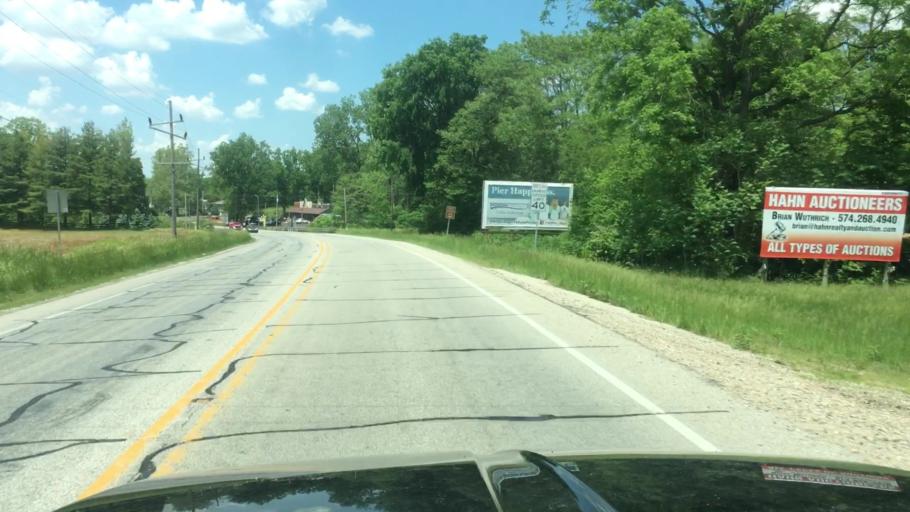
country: US
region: Indiana
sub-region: Kosciusko County
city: North Webster
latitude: 41.3150
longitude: -85.6914
